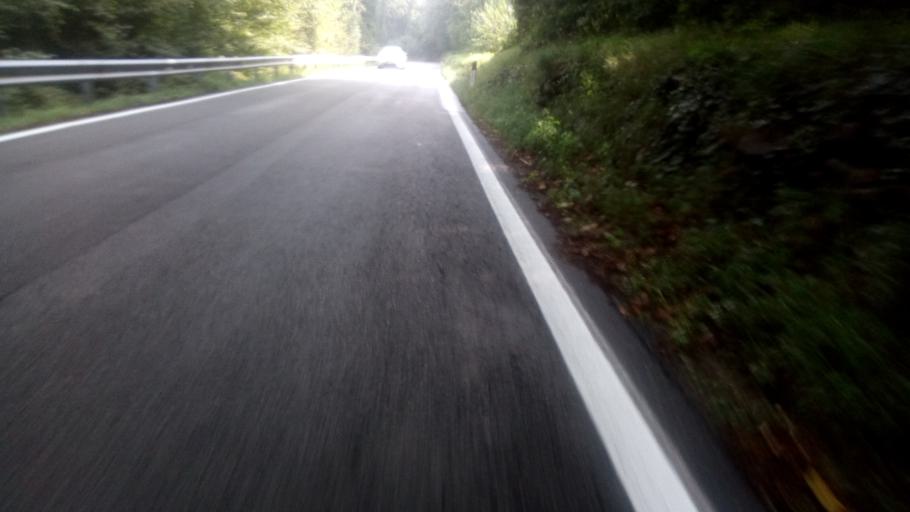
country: IT
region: Piedmont
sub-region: Provincia di Torino
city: Vistrorio
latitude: 45.4487
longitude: 7.7635
